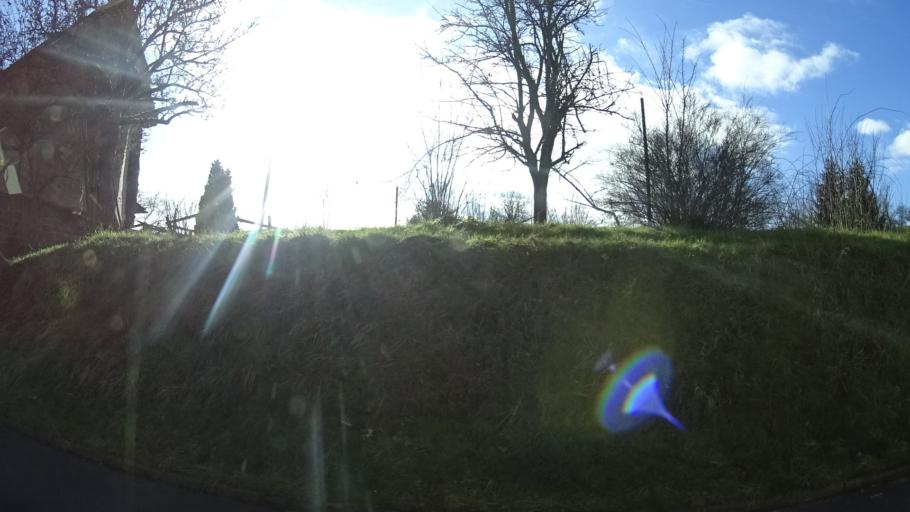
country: DE
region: Bavaria
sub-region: Regierungsbezirk Unterfranken
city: Neunkirchen
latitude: 49.8047
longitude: 9.4072
